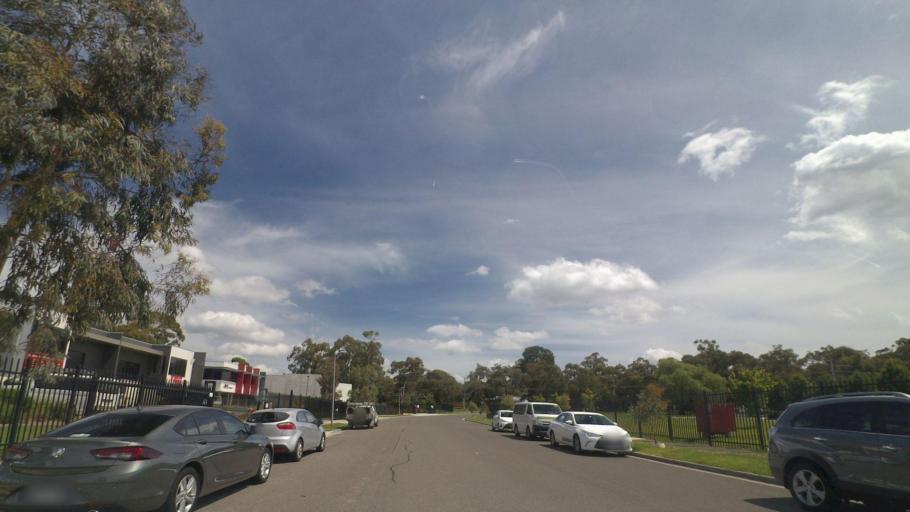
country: AU
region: Victoria
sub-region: Maroondah
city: Bayswater North
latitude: -37.8390
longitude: 145.2961
